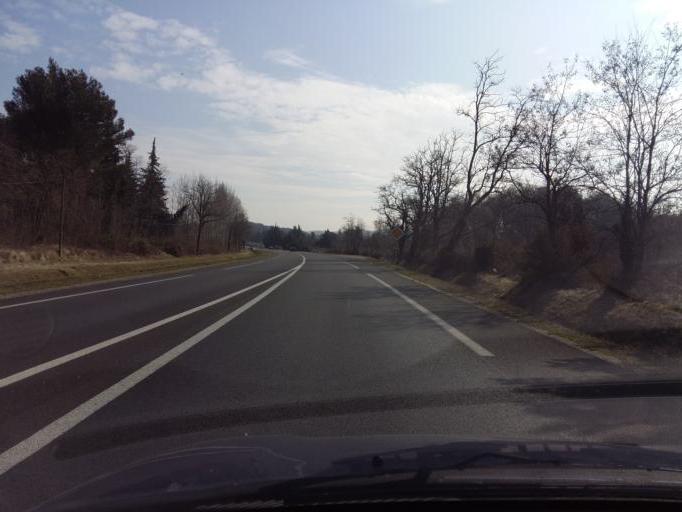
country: FR
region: Provence-Alpes-Cote d'Azur
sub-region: Departement des Bouches-du-Rhone
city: Orgon
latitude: 43.7965
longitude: 5.0120
